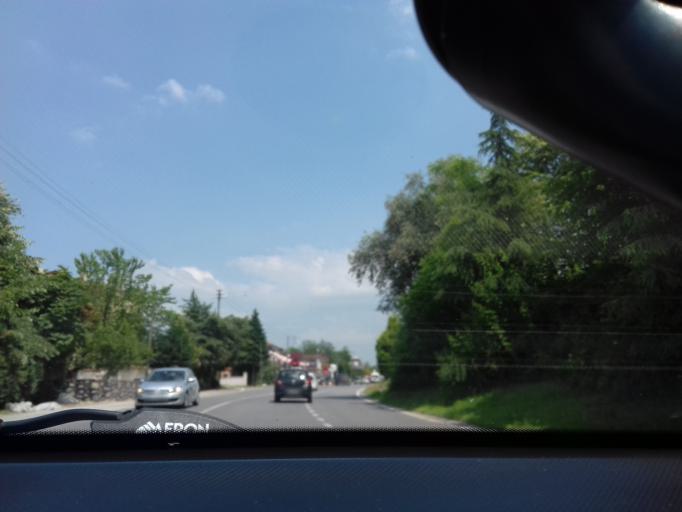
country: TR
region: Sakarya
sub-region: Merkez
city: Sapanca
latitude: 40.6910
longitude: 30.2278
